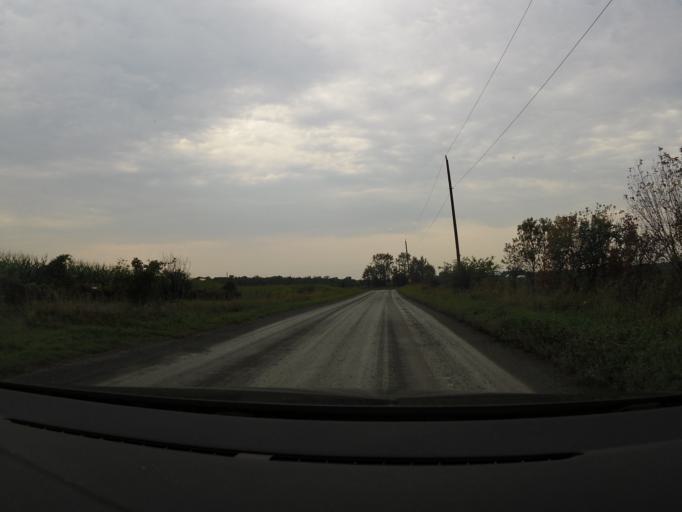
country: CA
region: Ontario
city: Carleton Place
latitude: 45.2010
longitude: -76.1203
